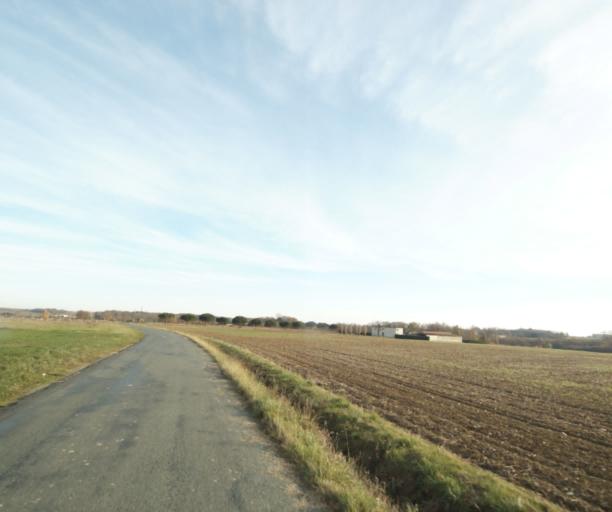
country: FR
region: Poitou-Charentes
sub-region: Departement de la Charente-Maritime
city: Chaniers
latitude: 45.7463
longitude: -0.5529
